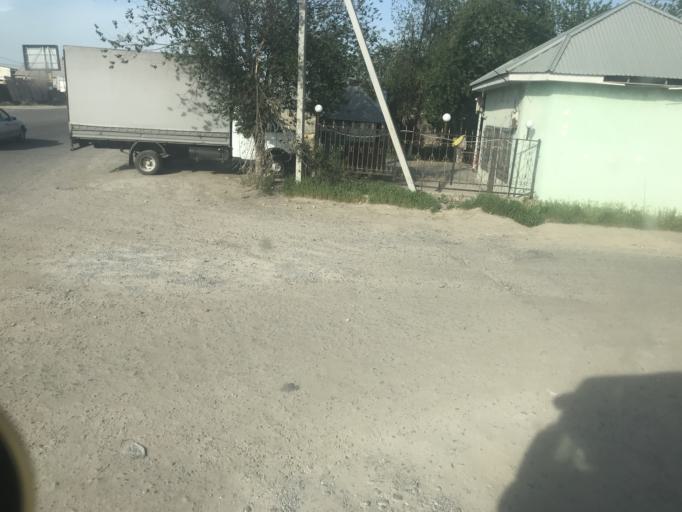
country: KZ
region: Ongtustik Qazaqstan
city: Shymkent
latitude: 42.3556
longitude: 69.5338
